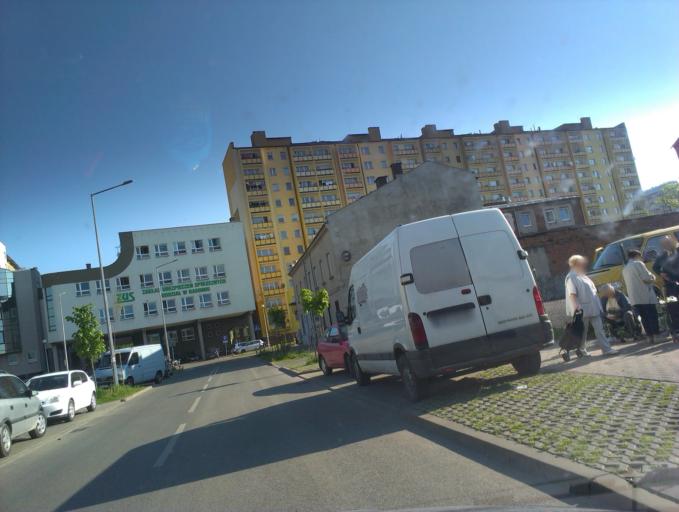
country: PL
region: Masovian Voivodeship
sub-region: Radom
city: Radom
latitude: 51.3977
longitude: 21.1645
